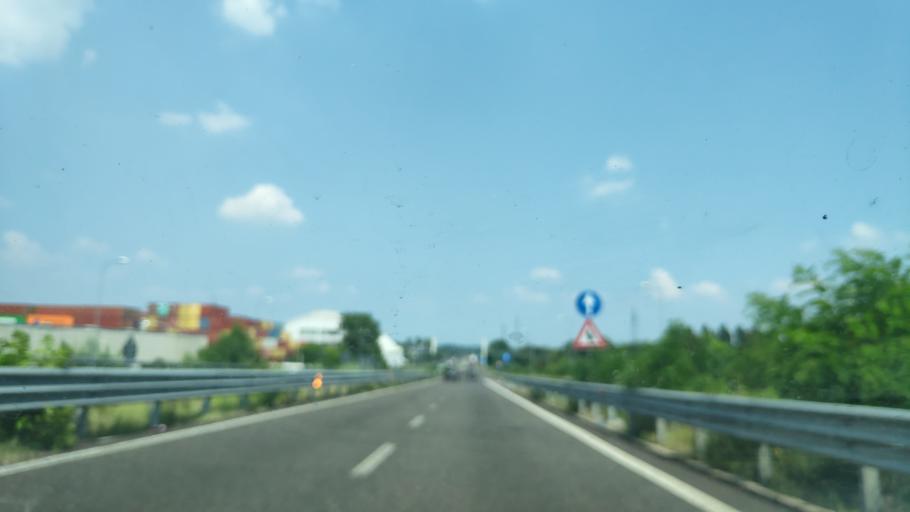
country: IT
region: Lombardy
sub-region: Citta metropolitana di Milano
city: San Bovio-San Felice
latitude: 45.4785
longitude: 9.3150
